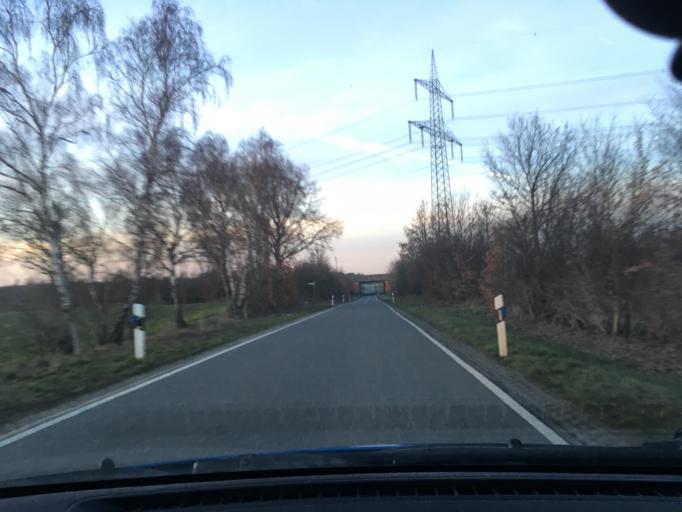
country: DE
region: Schleswig-Holstein
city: Besenthal
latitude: 53.5328
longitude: 10.7420
